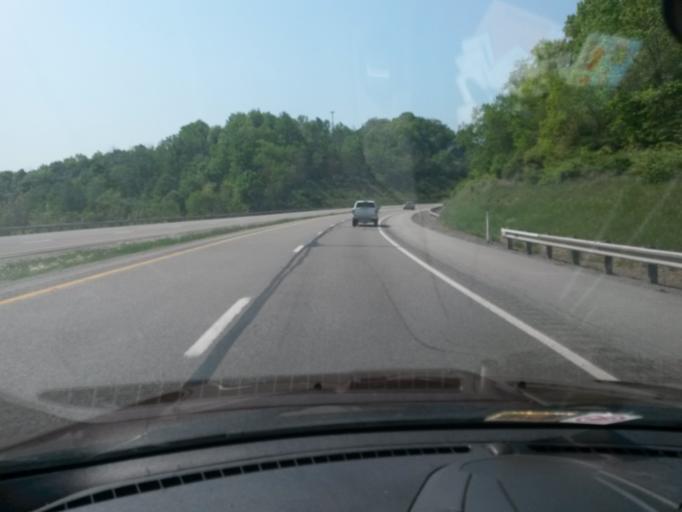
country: US
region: West Virginia
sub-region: Lewis County
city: Weston
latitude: 38.9311
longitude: -80.5439
